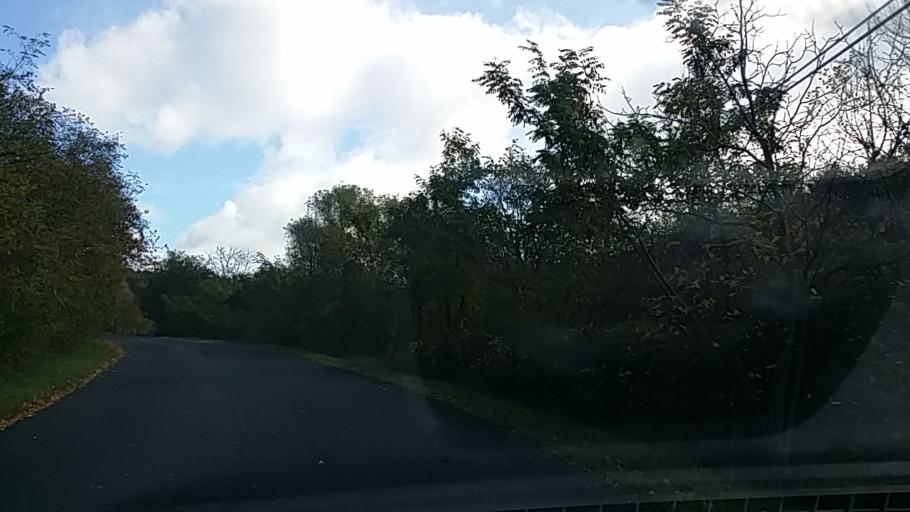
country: HU
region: Borsod-Abauj-Zemplen
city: Gonc
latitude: 48.3897
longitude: 21.2947
